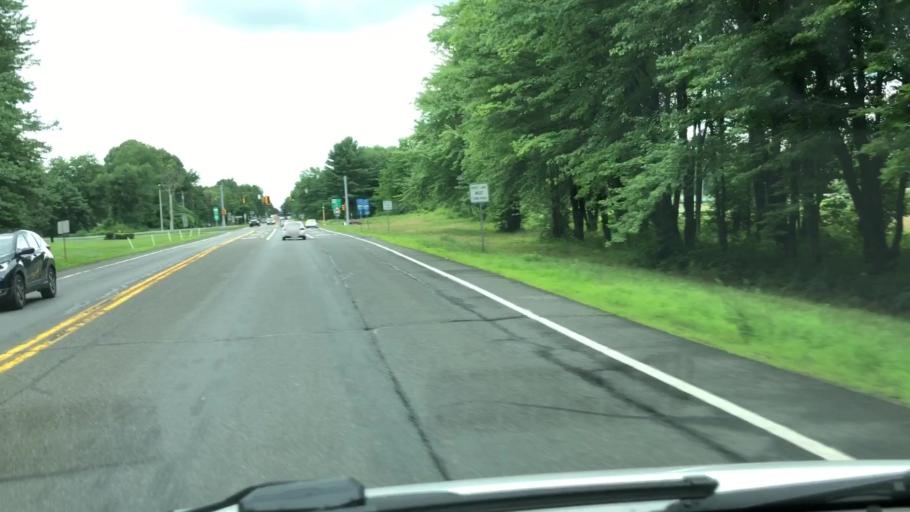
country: US
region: Massachusetts
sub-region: Franklin County
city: South Deerfield
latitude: 42.4840
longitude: -72.6124
